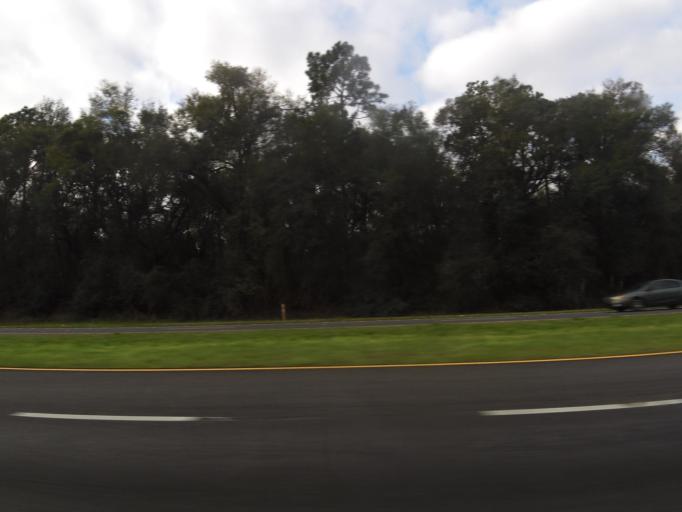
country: US
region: Florida
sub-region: Volusia County
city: Orange City
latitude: 28.9595
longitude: -81.2645
